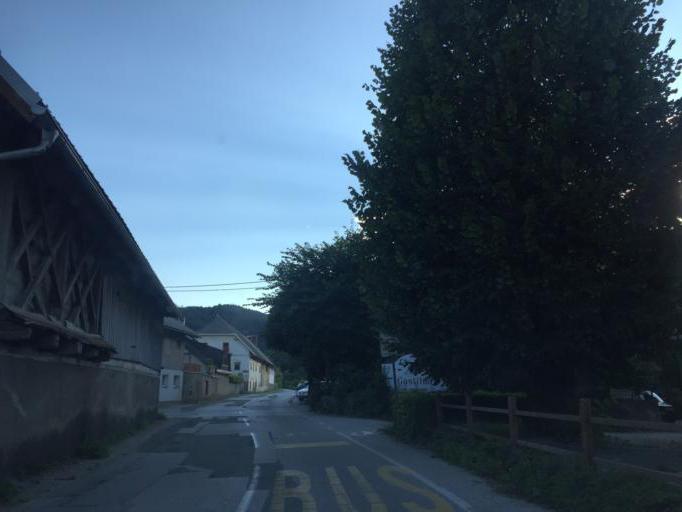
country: SI
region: Bled
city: Bled
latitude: 46.3753
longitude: 14.0930
